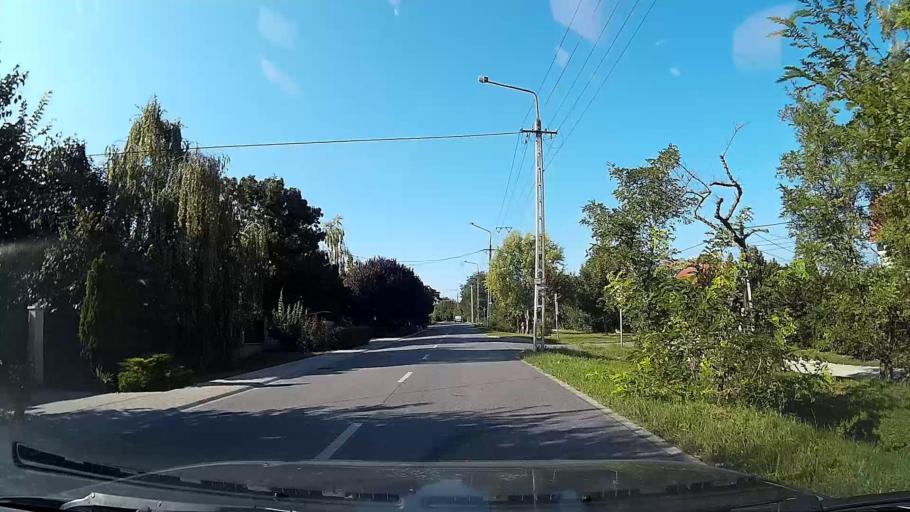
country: HU
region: Budapest
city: Budapest XXII. keruelet
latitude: 47.4200
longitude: 19.0065
